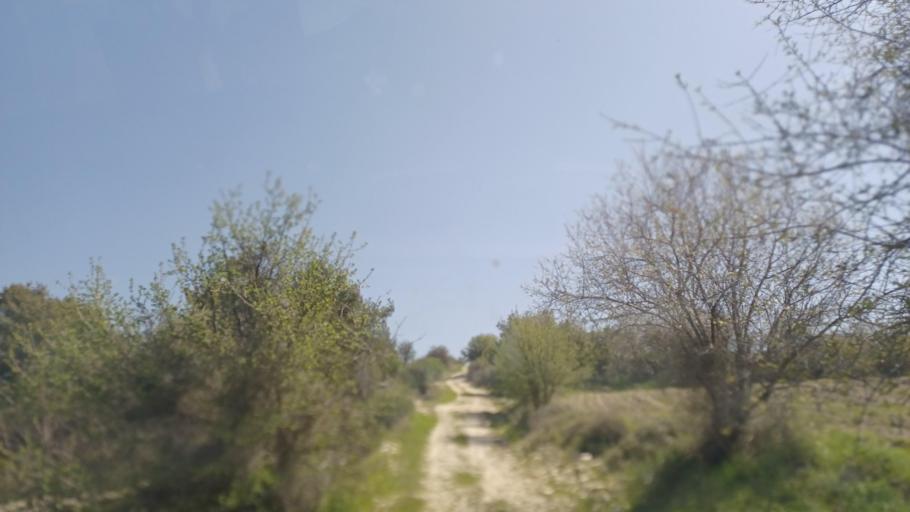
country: CY
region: Limassol
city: Pachna
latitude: 34.8628
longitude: 32.7470
